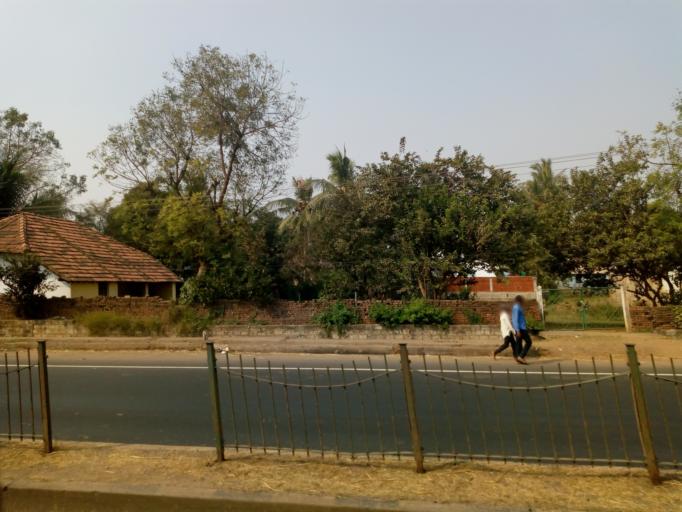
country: IN
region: Andhra Pradesh
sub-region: West Godavari
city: Eluru
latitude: 16.6336
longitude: 80.9608
